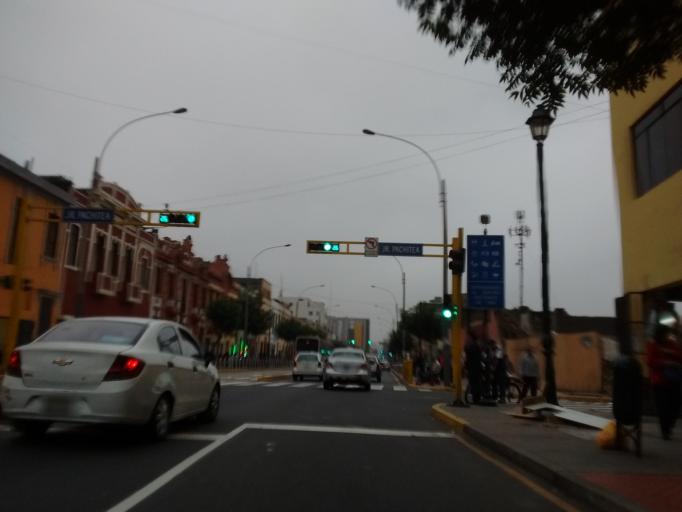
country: PE
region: Lima
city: Lima
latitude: -12.0547
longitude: -77.0343
